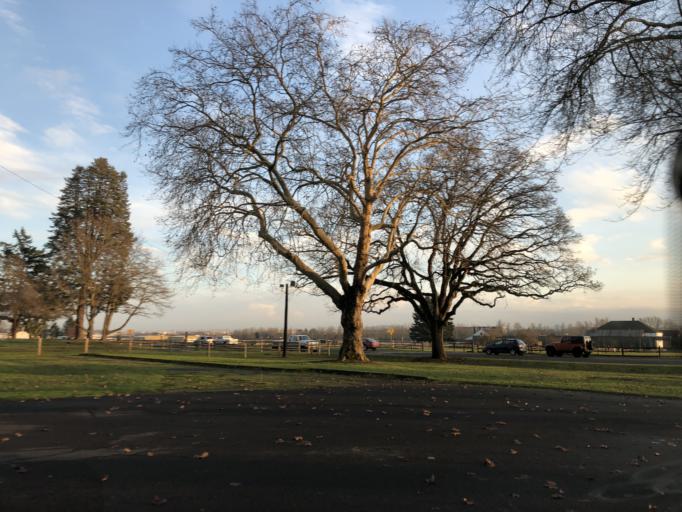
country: US
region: Washington
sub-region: Clark County
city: Vancouver
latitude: 45.6250
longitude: -122.6627
